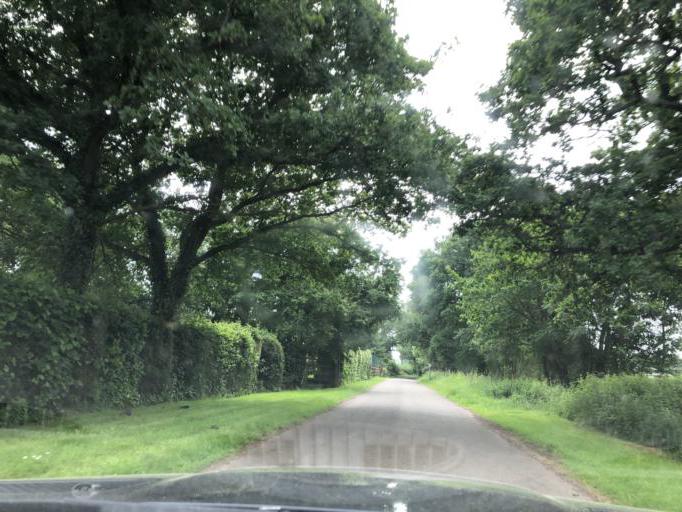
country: GB
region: England
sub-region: Warwickshire
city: Wroxall
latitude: 52.3428
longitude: -1.6442
